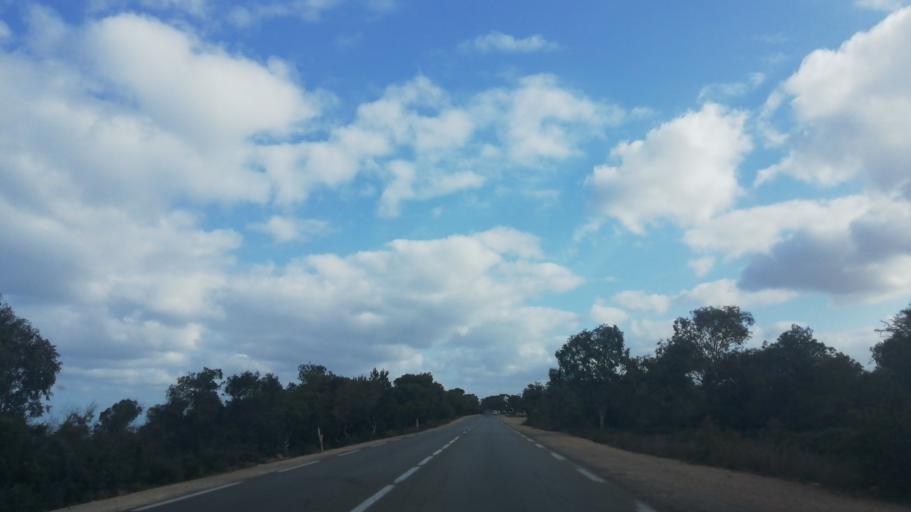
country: DZ
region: Relizane
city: Mazouna
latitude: 36.2359
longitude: 0.5237
